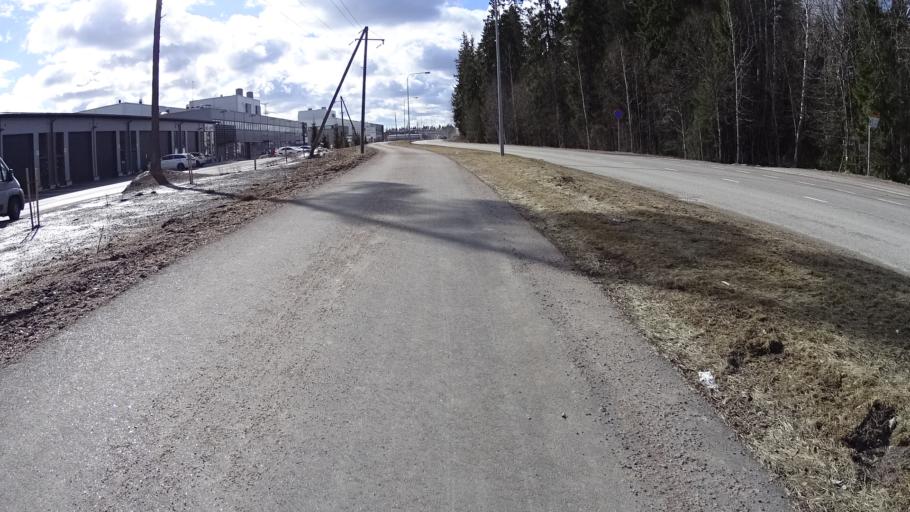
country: FI
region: Uusimaa
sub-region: Helsinki
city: Kauniainen
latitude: 60.2632
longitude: 24.7235
